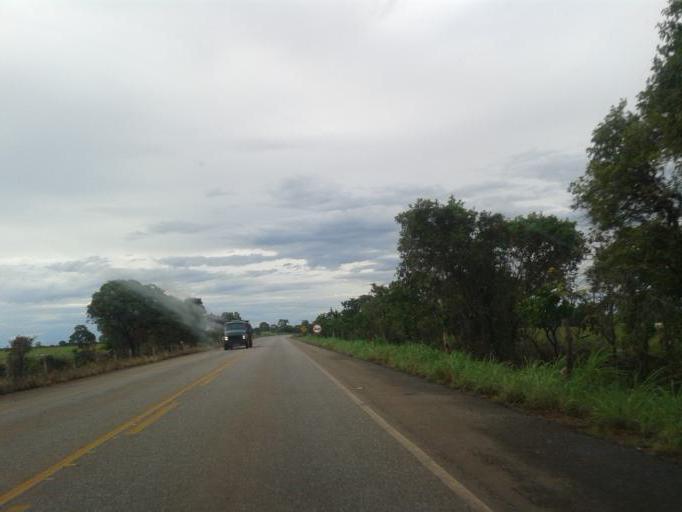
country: BR
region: Goias
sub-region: Mozarlandia
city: Mozarlandia
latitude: -14.8013
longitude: -50.5344
